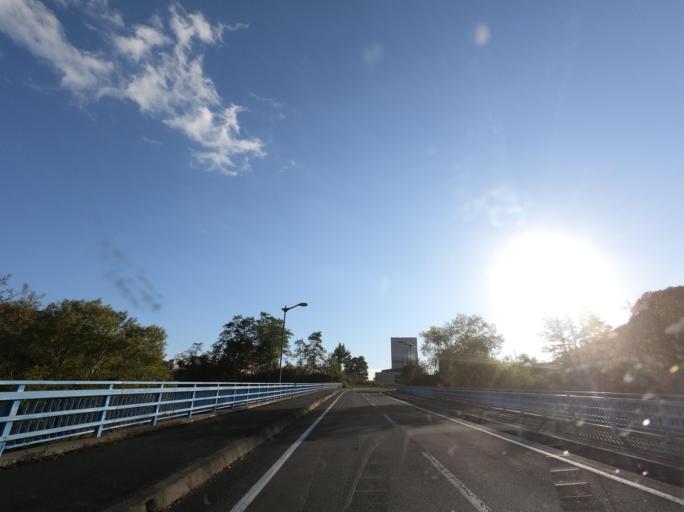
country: JP
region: Hokkaido
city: Iwamizawa
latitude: 43.0531
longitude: 141.9700
